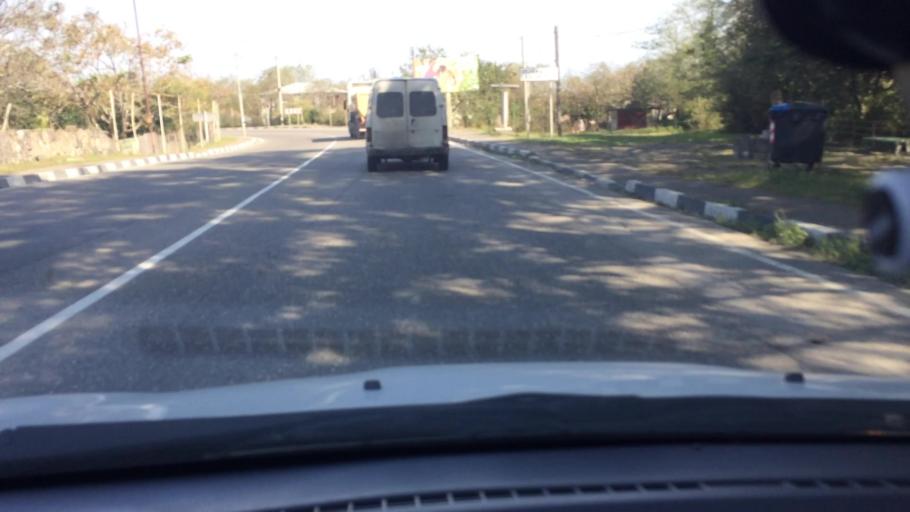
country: GE
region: Guria
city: Lanchkhuti
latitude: 42.0795
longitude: 42.0508
